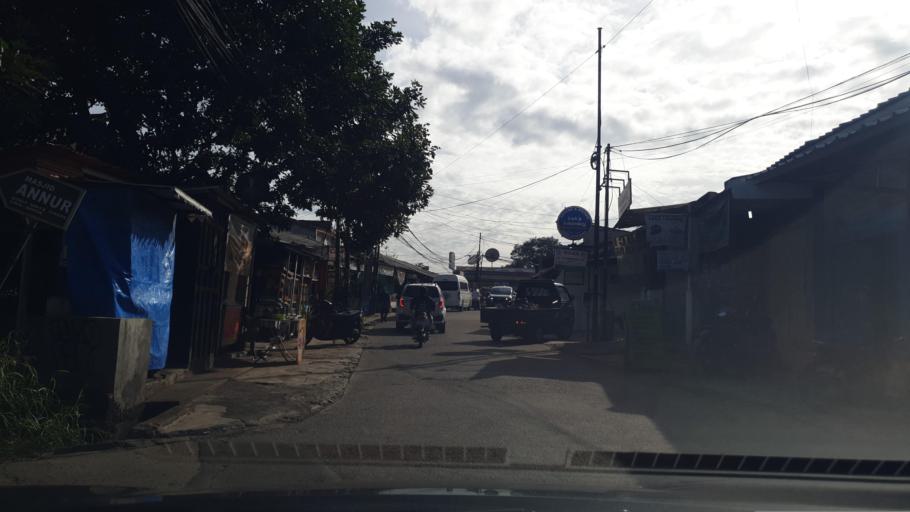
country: ID
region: West Java
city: Sawangan
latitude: -6.3603
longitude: 106.7798
